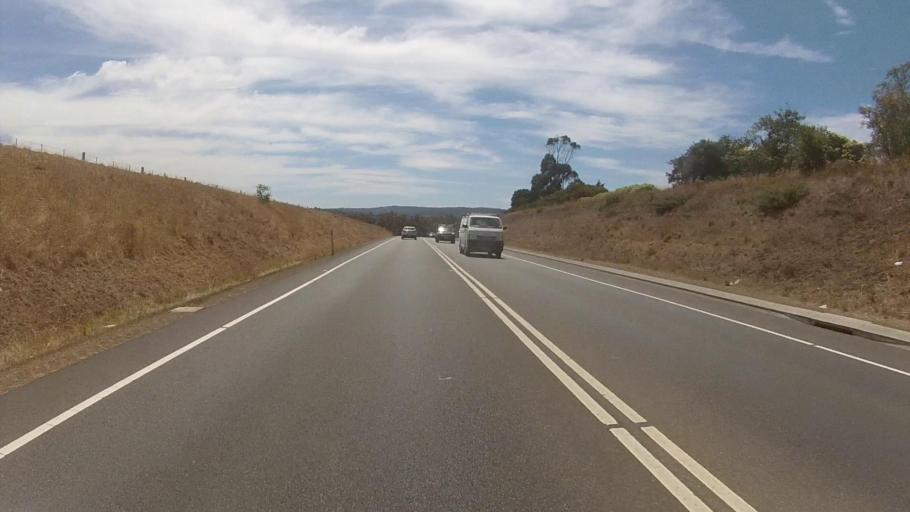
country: AU
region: Tasmania
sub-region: Kingborough
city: Kingston
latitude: -42.9901
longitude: 147.2855
